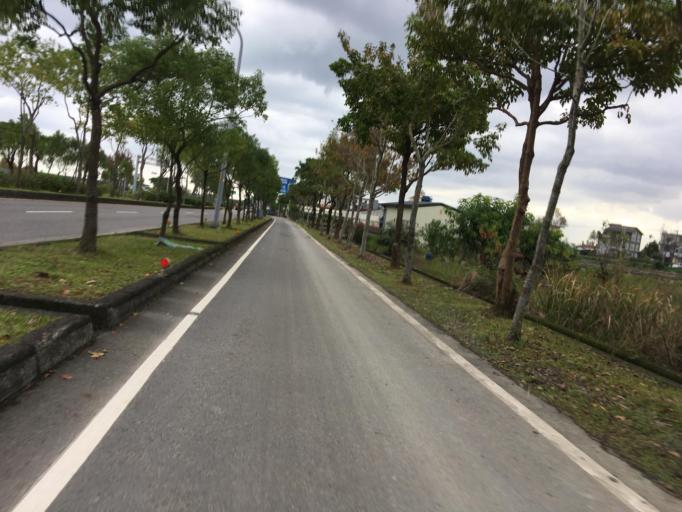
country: TW
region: Taiwan
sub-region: Yilan
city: Yilan
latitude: 24.7697
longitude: 121.7718
